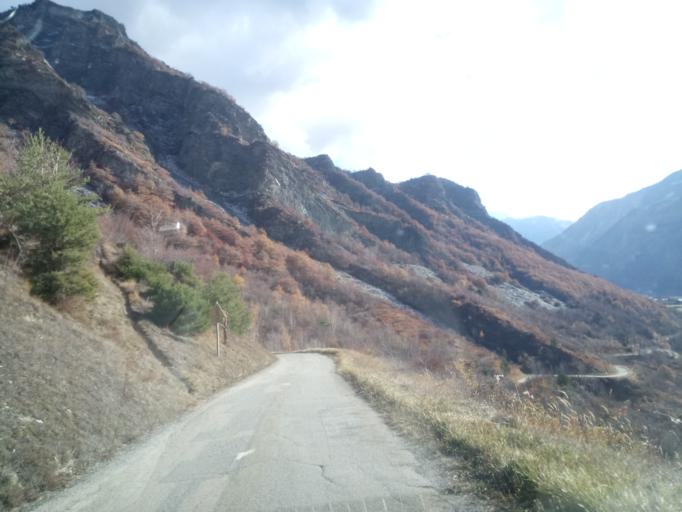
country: FR
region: Rhone-Alpes
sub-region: Departement de la Savoie
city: Villargondran
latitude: 45.2673
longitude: 6.3886
